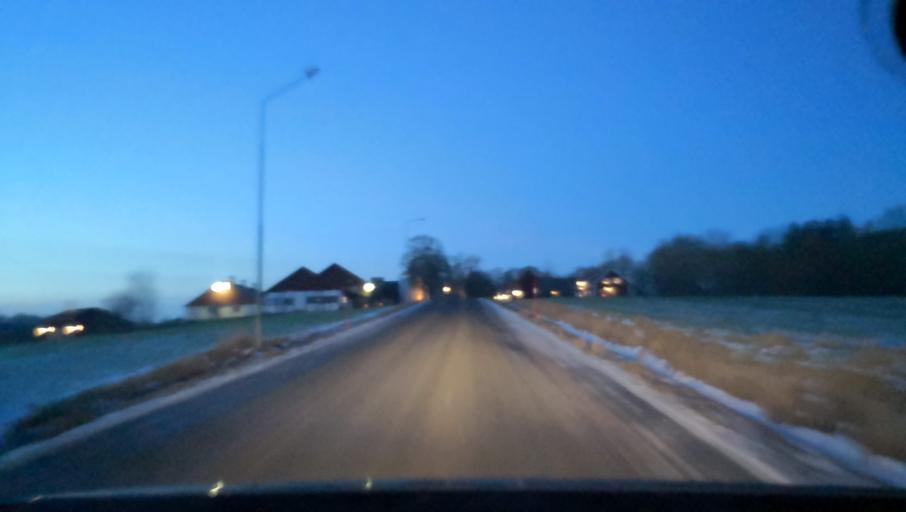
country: SE
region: Soedermanland
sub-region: Katrineholms Kommun
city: Katrineholm
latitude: 59.0678
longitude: 16.3581
